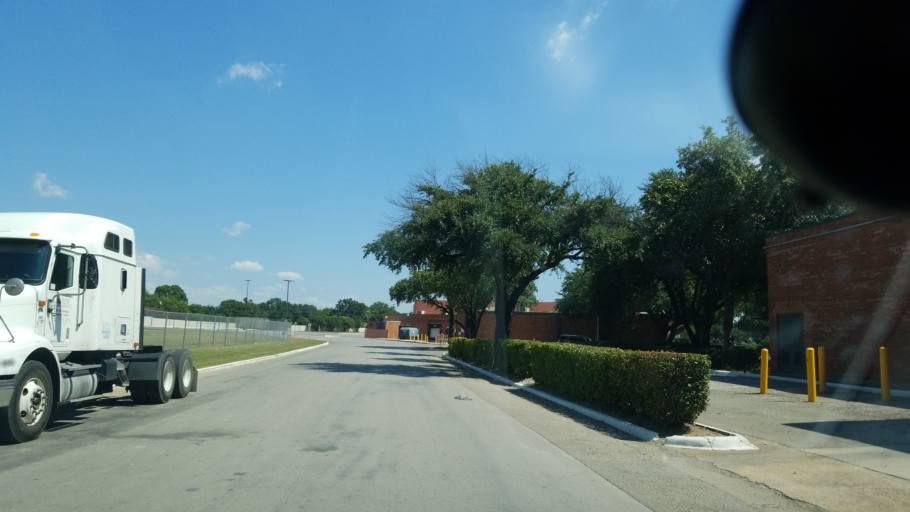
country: US
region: Texas
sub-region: Dallas County
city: Cockrell Hill
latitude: 32.7226
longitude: -96.8354
